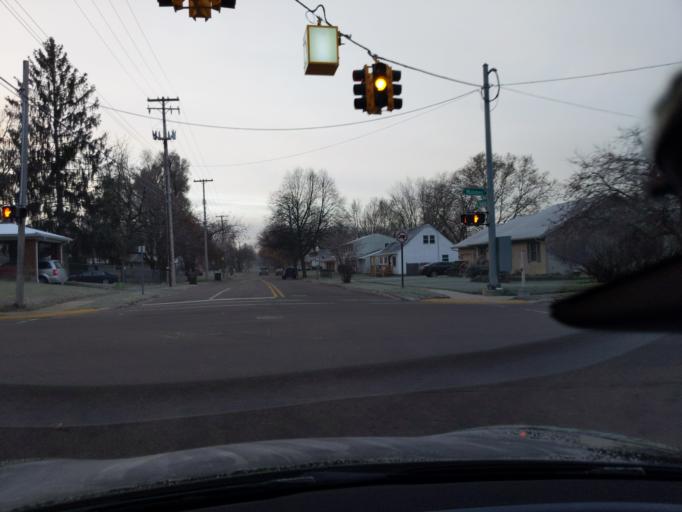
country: US
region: Michigan
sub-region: Ingham County
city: Lansing
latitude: 42.6975
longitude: -84.5527
